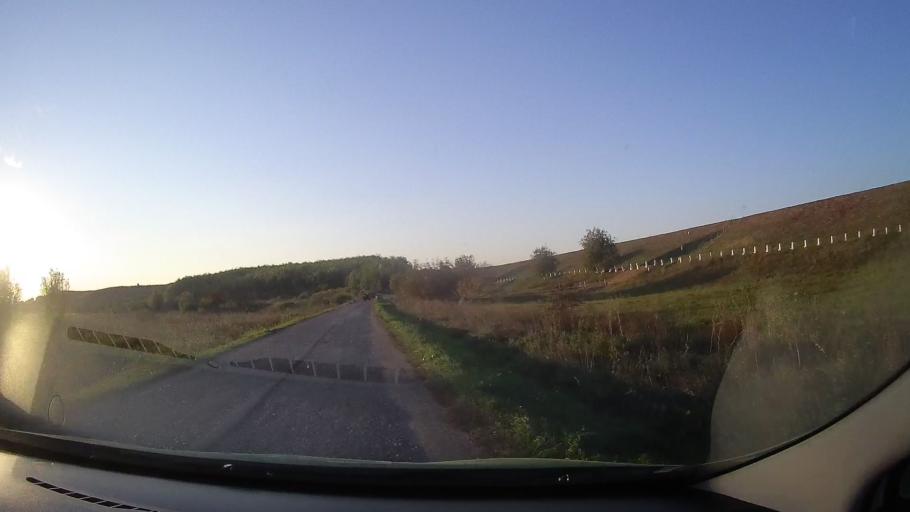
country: RO
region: Bihor
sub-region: Comuna Salard
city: Salard
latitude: 47.2504
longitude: 22.0303
